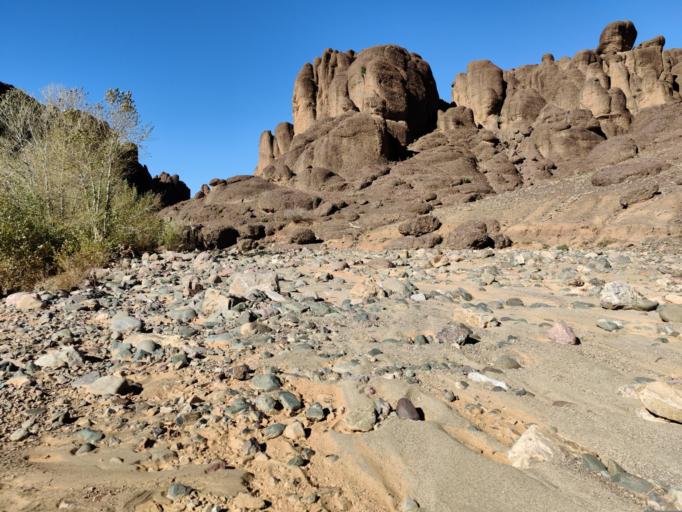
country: MA
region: Souss-Massa-Draa
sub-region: Taroudannt
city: Taliouine
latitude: 30.5541
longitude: -7.5871
